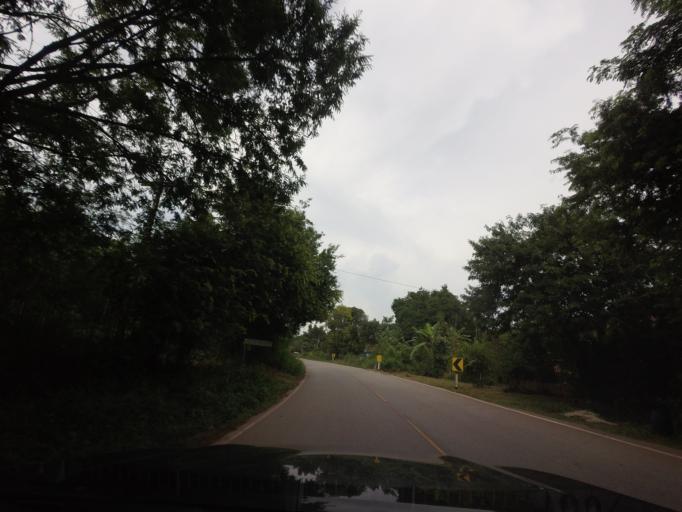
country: TH
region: Changwat Nong Bua Lamphu
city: Suwannakhuha
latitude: 17.4482
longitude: 102.3447
